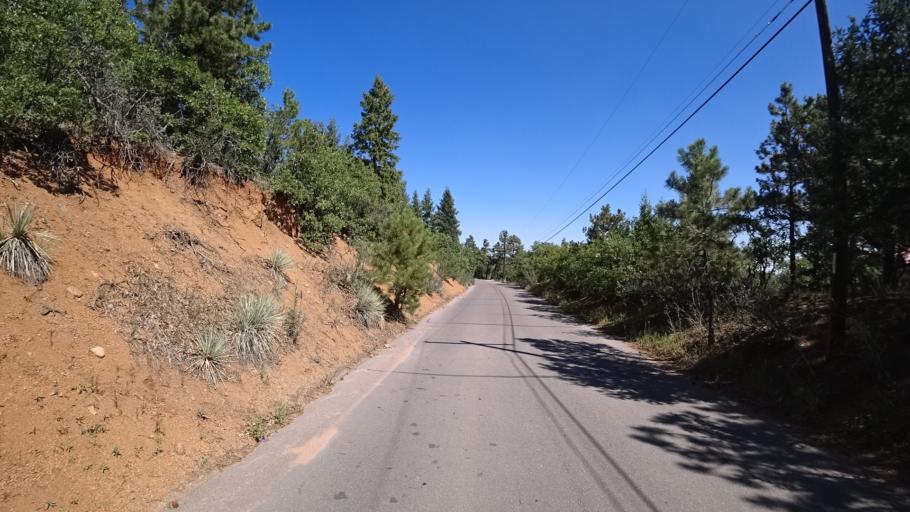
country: US
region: Colorado
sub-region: El Paso County
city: Colorado Springs
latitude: 38.8072
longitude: -104.8784
